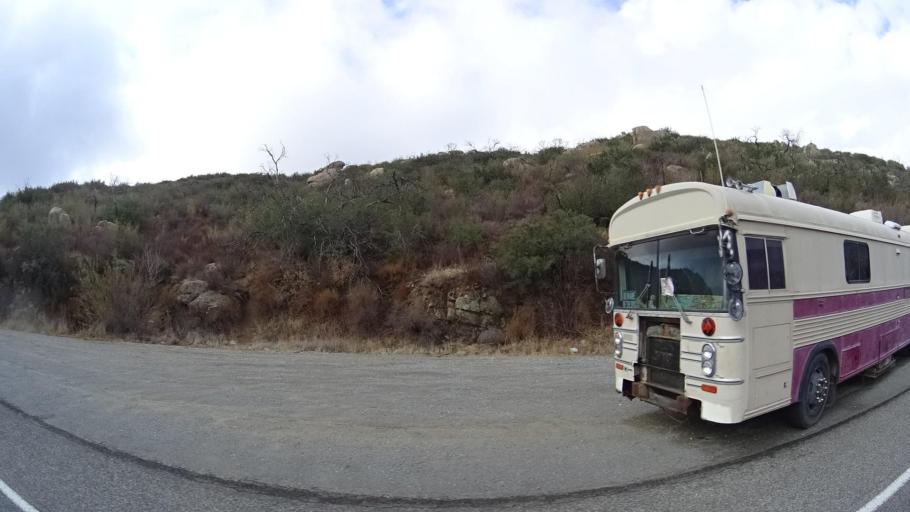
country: MX
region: Baja California
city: Tecate
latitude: 32.6022
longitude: -116.6033
